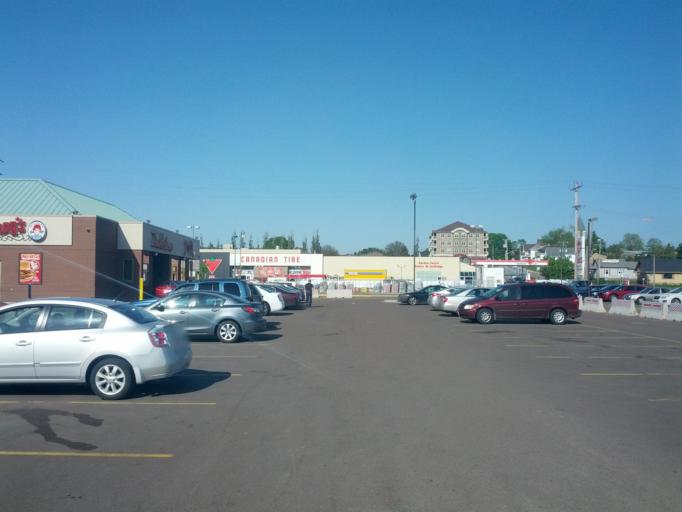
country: CA
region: New Brunswick
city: Moncton
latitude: 46.0965
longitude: -64.7583
